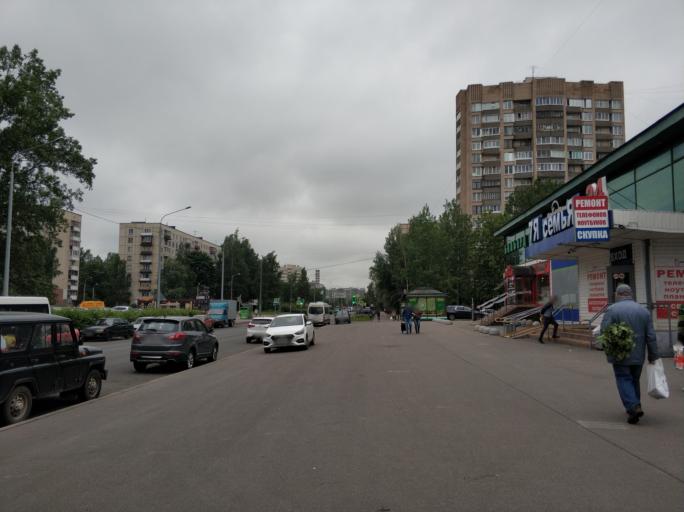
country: RU
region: St.-Petersburg
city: Grazhdanka
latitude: 60.0407
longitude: 30.4145
